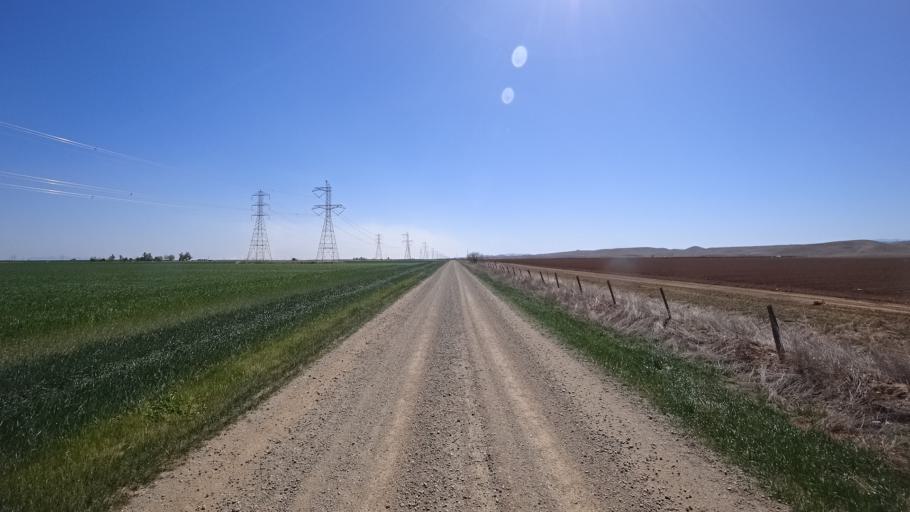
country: US
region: California
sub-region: Glenn County
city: Willows
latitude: 39.4708
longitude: -122.2865
